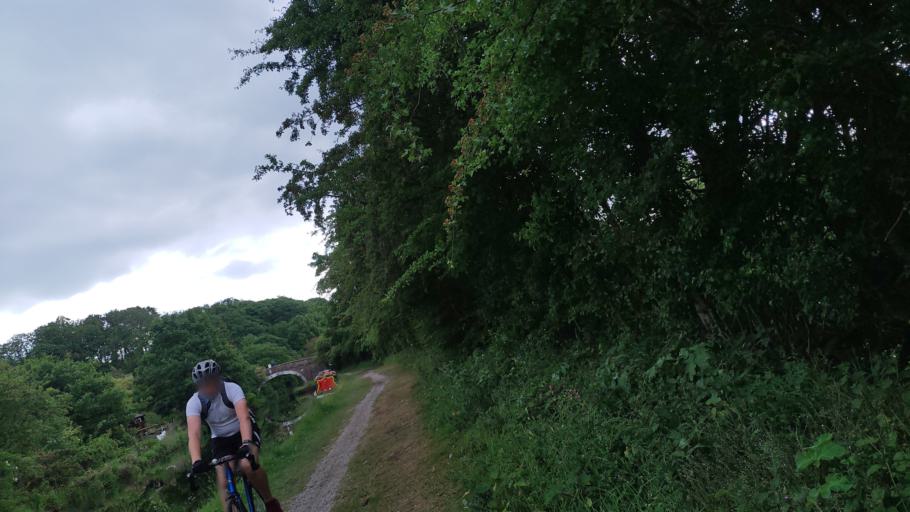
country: GB
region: England
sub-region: Lancashire
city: Chorley
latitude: 53.6927
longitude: -2.6053
